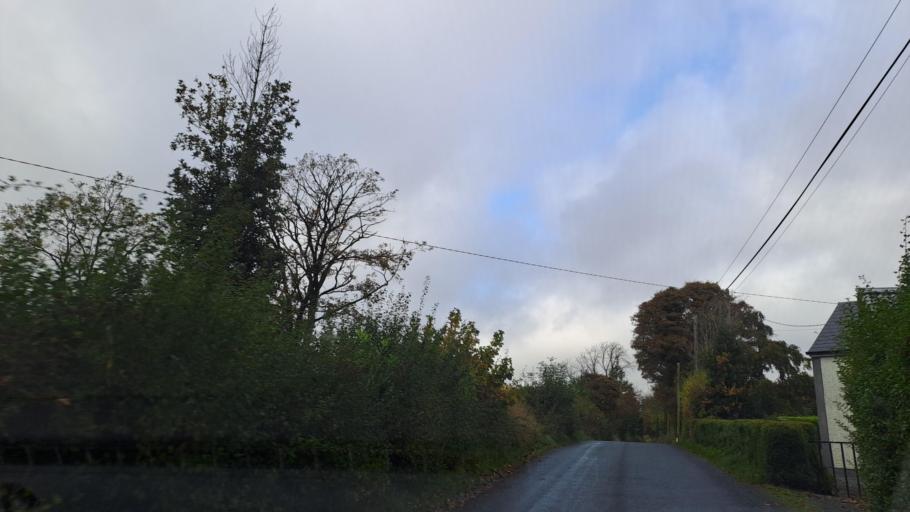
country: IE
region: Ulster
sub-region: An Cabhan
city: Bailieborough
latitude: 53.9897
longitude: -7.0039
